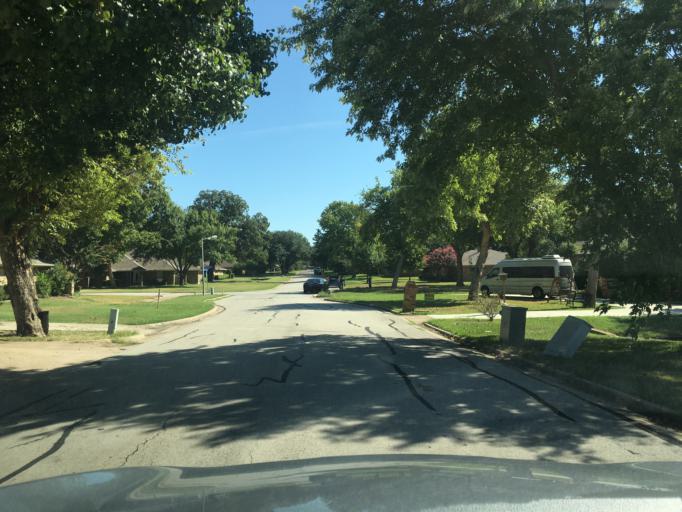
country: US
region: Texas
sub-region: Dallas County
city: Sachse
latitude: 32.9696
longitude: -96.6079
